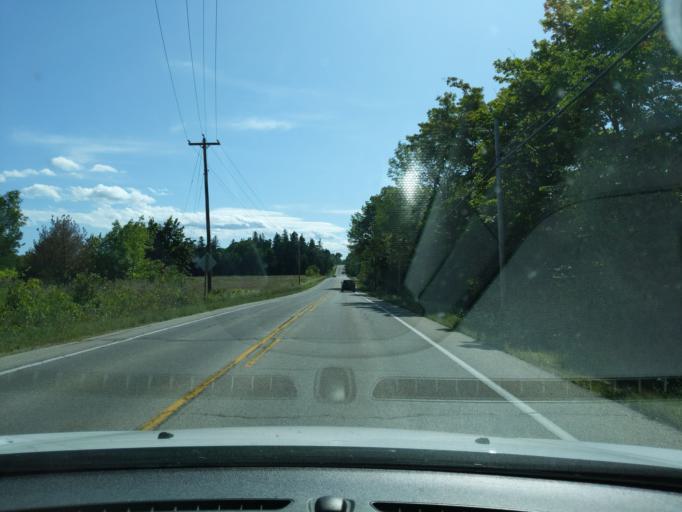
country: US
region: Wisconsin
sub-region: Door County
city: Sturgeon Bay
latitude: 45.2218
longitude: -87.1064
